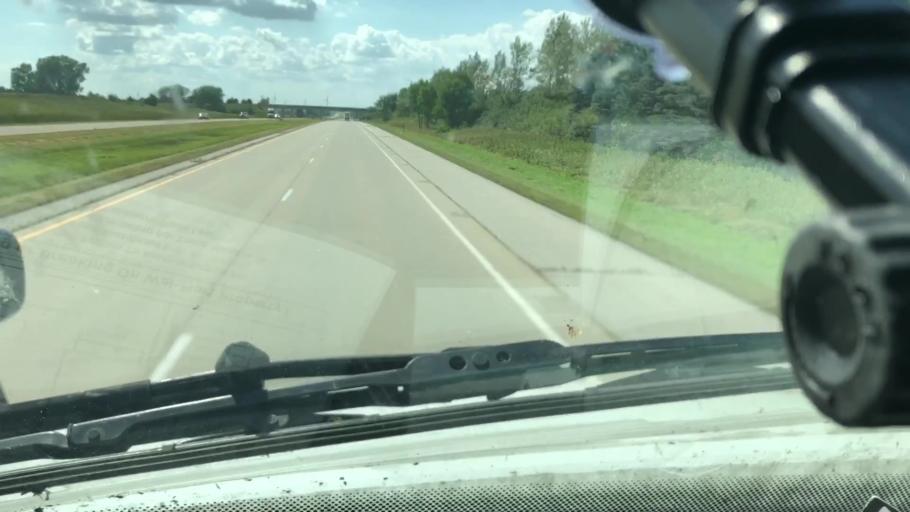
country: US
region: Minnesota
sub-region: Mower County
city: Grand Meadow
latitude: 43.7795
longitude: -92.6213
